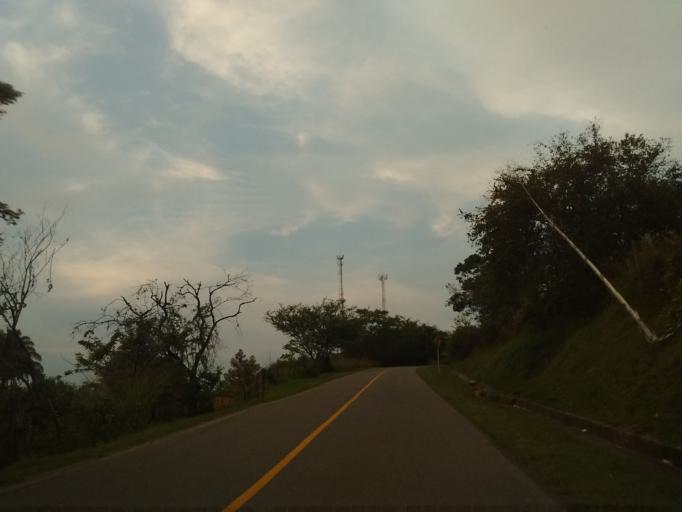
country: CO
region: Cauca
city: Caloto
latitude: 3.0675
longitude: -76.3538
